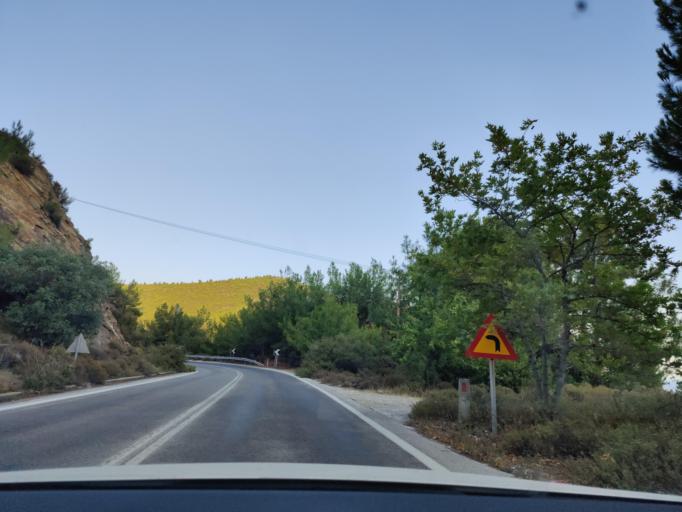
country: GR
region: East Macedonia and Thrace
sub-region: Nomos Kavalas
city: Potamia
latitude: 40.6217
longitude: 24.7597
